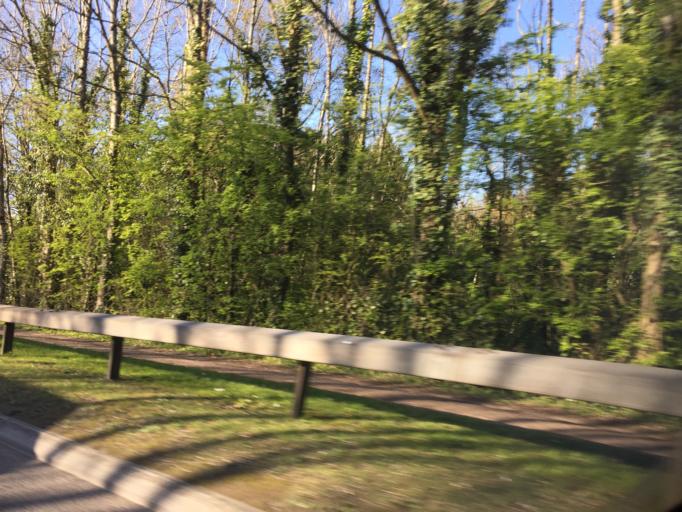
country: GB
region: Wales
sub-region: Torfaen County Borough
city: Cwmbran
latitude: 51.6240
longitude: -3.0130
